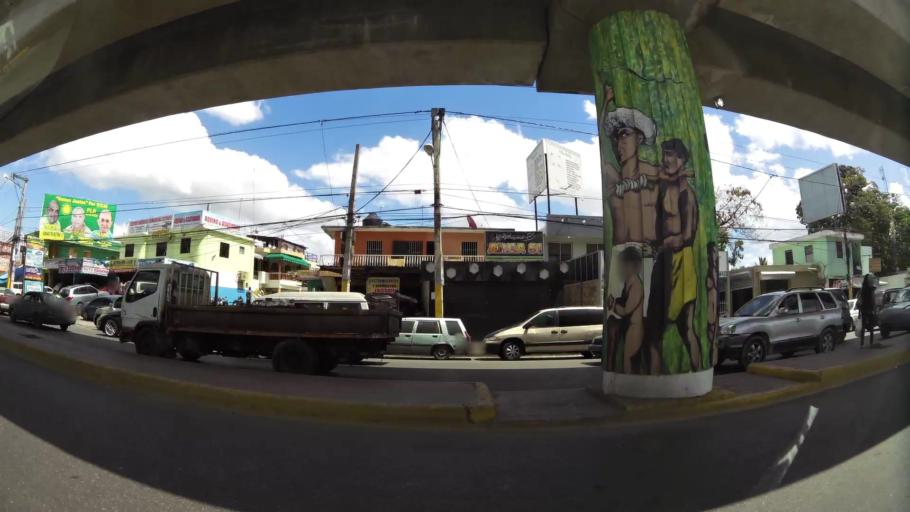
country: DO
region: Nacional
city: La Agustina
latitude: 18.5216
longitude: -69.9168
